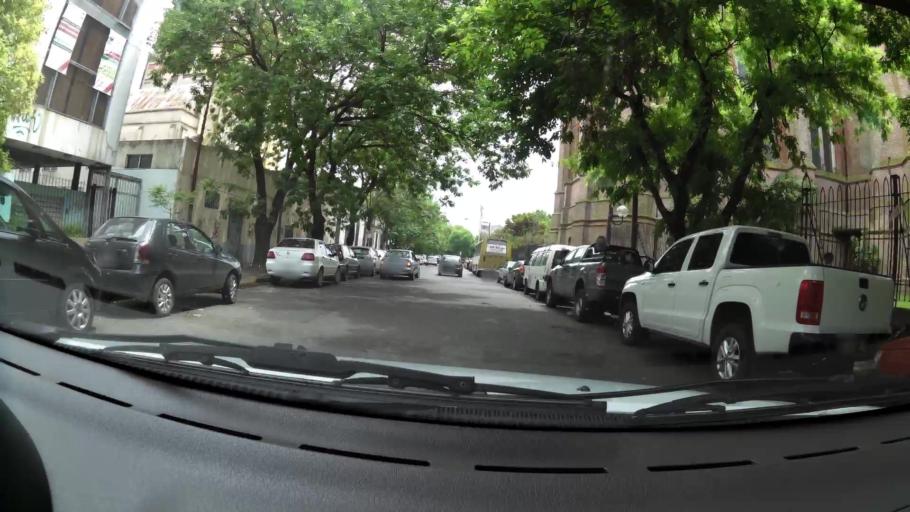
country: AR
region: Buenos Aires
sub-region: Partido de La Plata
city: La Plata
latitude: -34.9235
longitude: -57.9564
